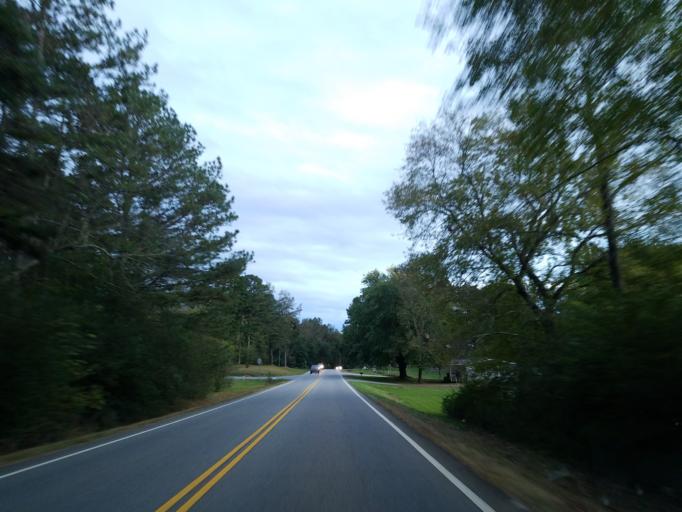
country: US
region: Georgia
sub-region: Dawson County
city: Dawsonville
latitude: 34.3864
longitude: -84.1254
